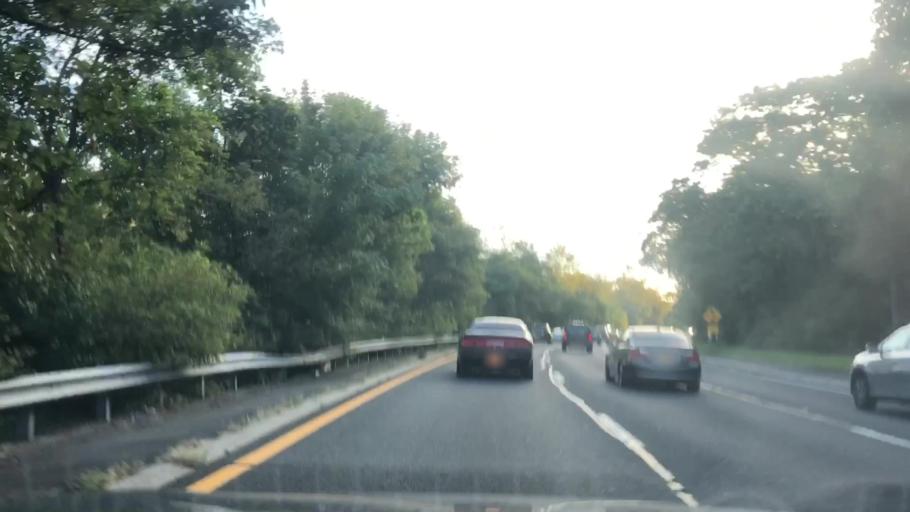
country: US
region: New York
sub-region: Nassau County
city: Uniondale
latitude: 40.6908
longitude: -73.5877
